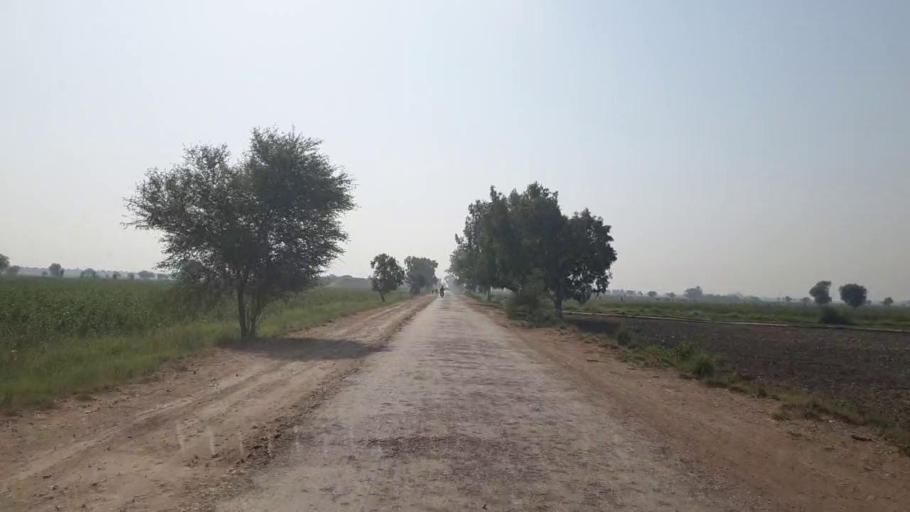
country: PK
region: Sindh
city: Shahdadpur
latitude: 25.9332
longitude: 68.7300
